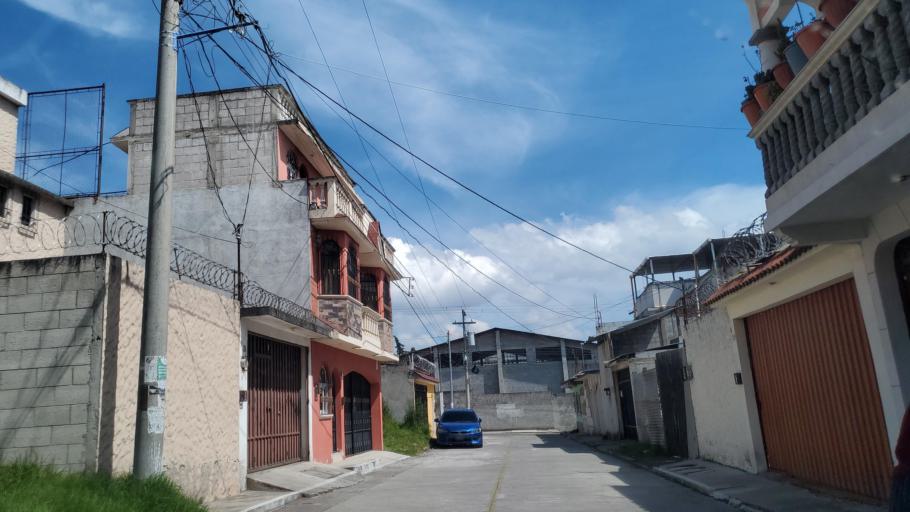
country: GT
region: Quetzaltenango
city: Quetzaltenango
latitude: 14.8307
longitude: -91.5384
